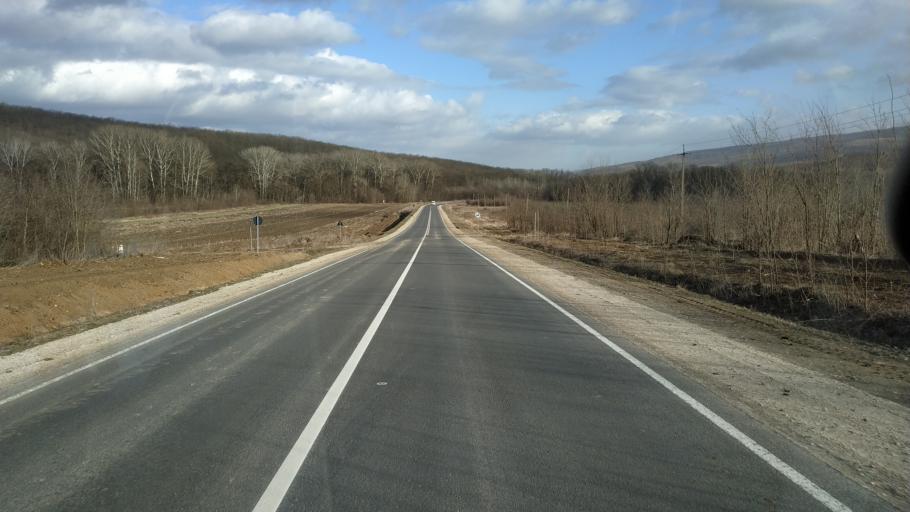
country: MD
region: Calarasi
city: Calarasi
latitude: 47.3073
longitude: 28.1304
